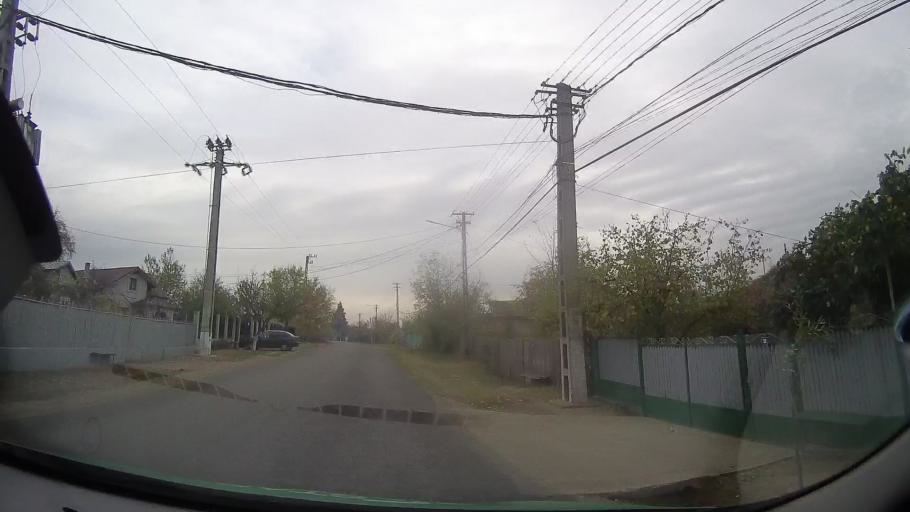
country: RO
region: Prahova
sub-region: Comuna Valea Calugareasca
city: Pantazi
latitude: 44.9324
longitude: 26.1416
